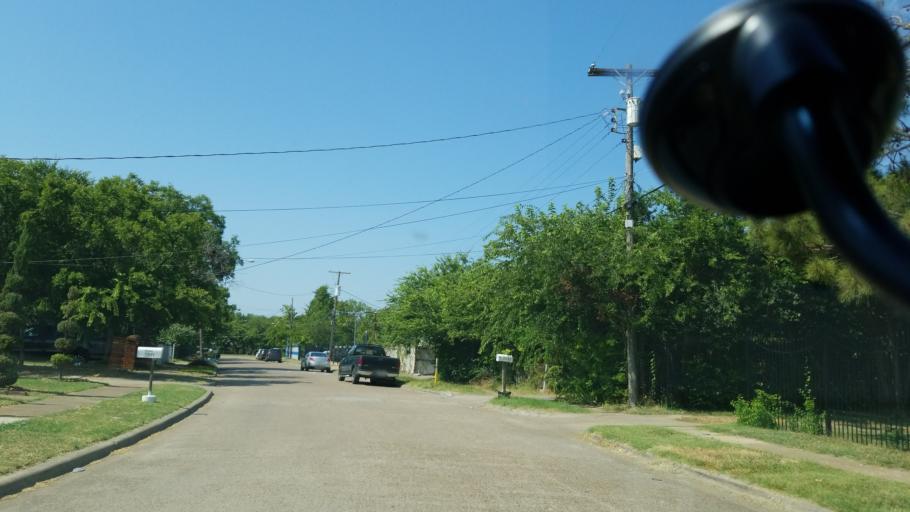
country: US
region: Texas
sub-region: Dallas County
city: Cockrell Hill
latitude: 32.7165
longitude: -96.8780
